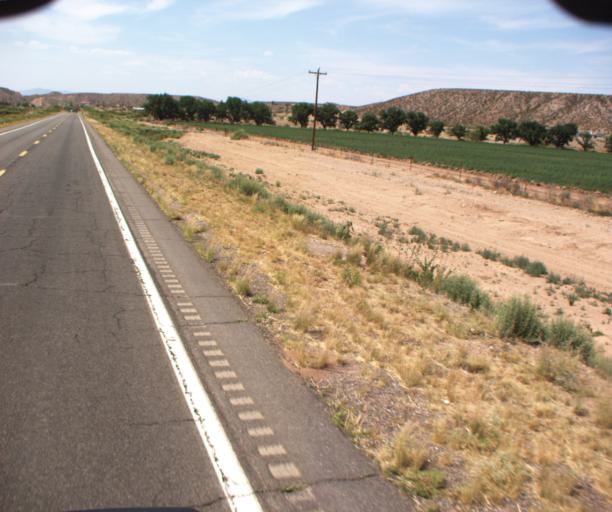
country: US
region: Arizona
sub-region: Greenlee County
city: Clifton
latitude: 32.8596
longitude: -109.1843
